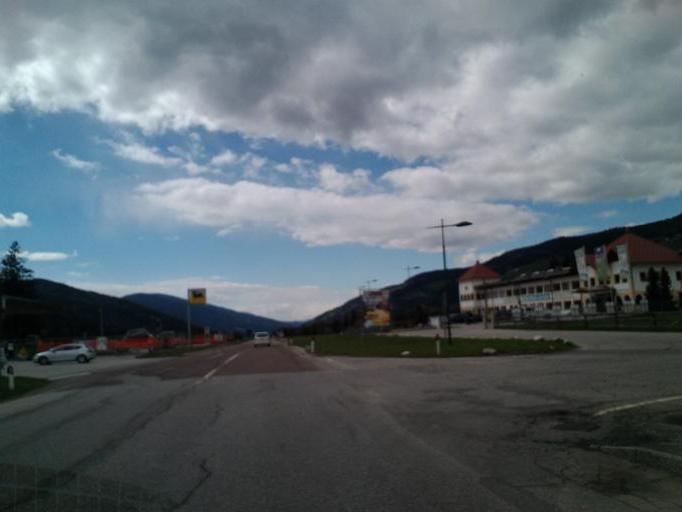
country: IT
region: Trentino-Alto Adige
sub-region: Bolzano
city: Dobbiaco
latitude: 46.7290
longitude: 12.2197
